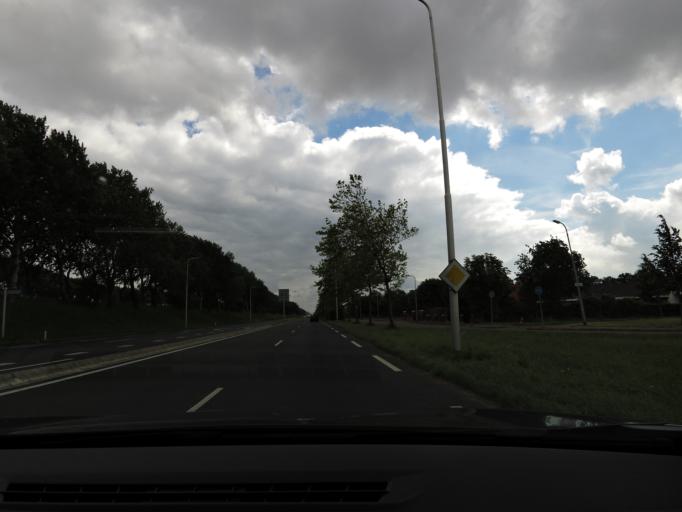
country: NL
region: Zeeland
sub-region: Gemeente Middelburg
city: Middelburg
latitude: 51.4805
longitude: 3.6014
